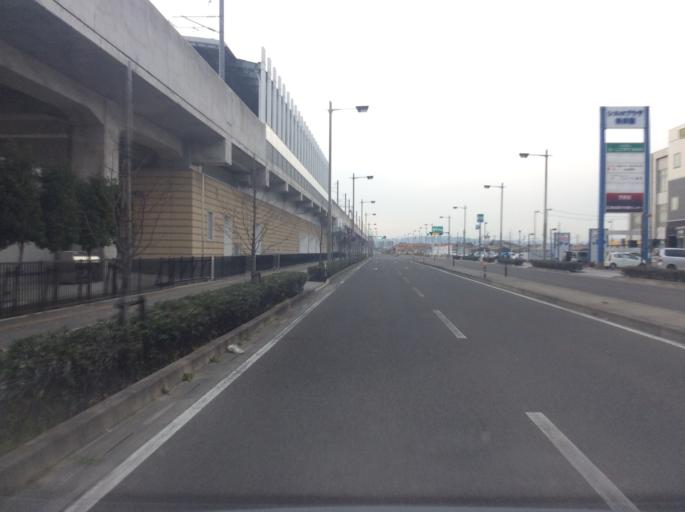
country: JP
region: Miyagi
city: Iwanuma
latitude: 38.1596
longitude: 140.9184
